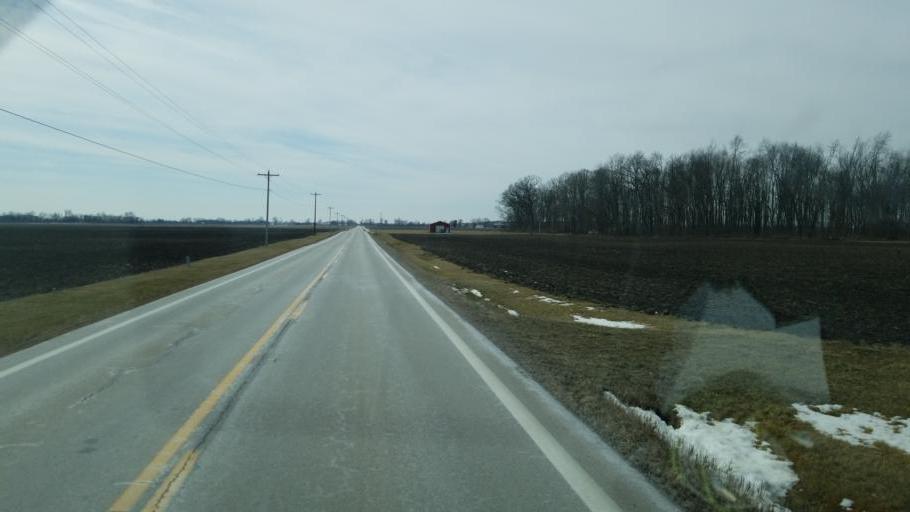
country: US
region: Ohio
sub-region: Delaware County
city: Delaware
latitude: 40.3195
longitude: -82.9883
